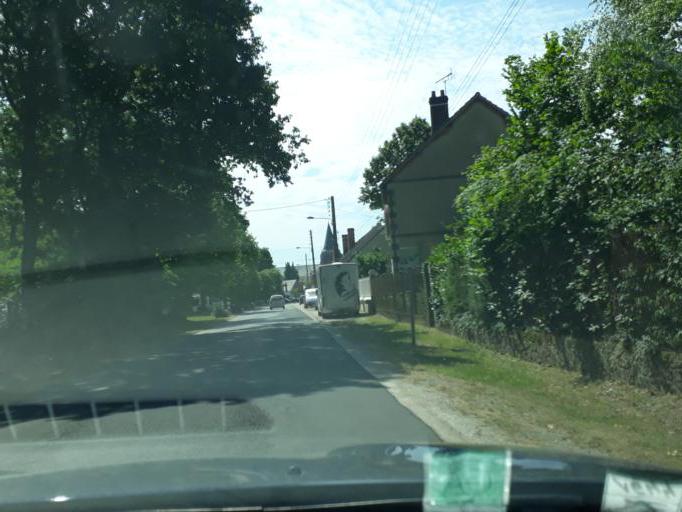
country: FR
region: Centre
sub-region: Departement du Loir-et-Cher
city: Vouzon
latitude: 47.6496
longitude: 2.0560
